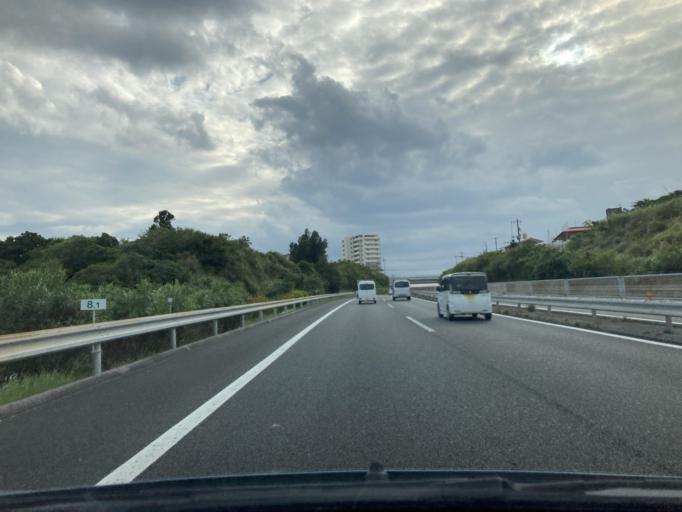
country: JP
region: Okinawa
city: Ginowan
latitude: 26.2603
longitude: 127.7705
